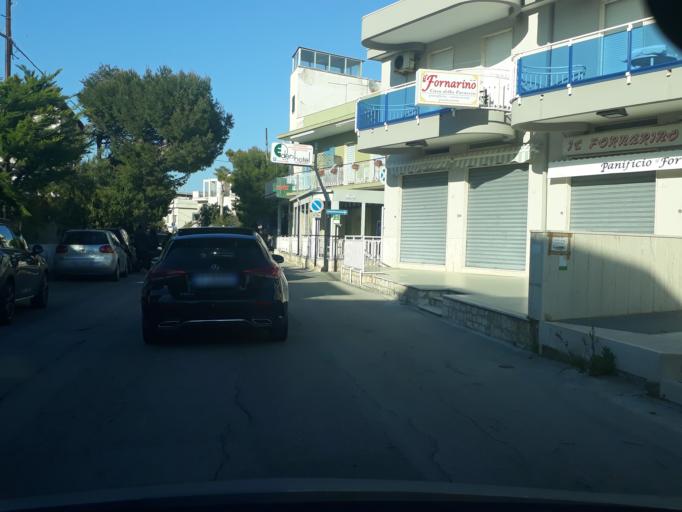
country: IT
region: Apulia
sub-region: Provincia di Brindisi
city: Pezze di Greco
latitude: 40.8369
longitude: 17.4658
